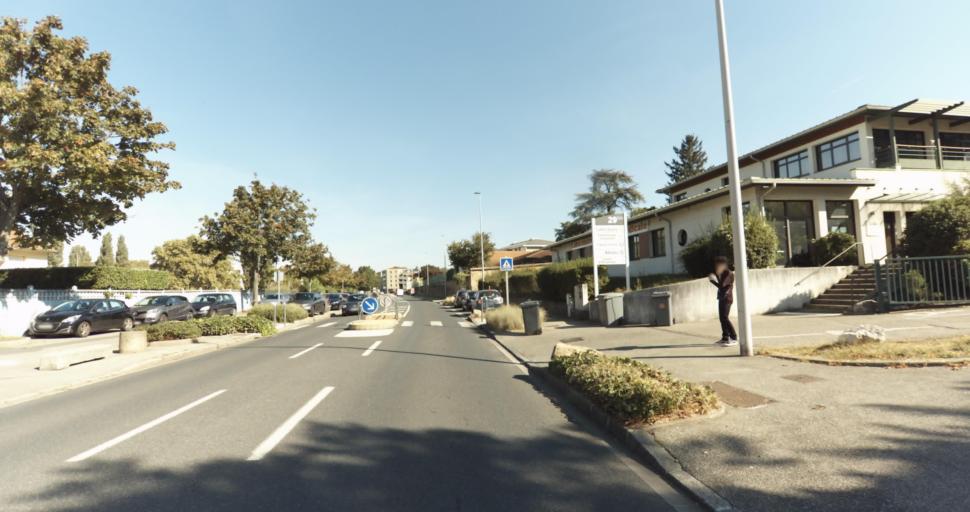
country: FR
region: Rhone-Alpes
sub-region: Departement du Rhone
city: Albigny-sur-Saone
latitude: 45.8693
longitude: 4.8398
